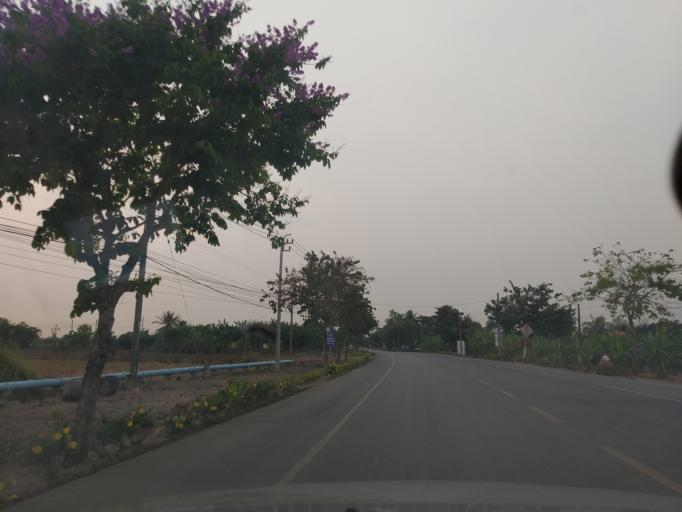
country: TH
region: Bangkok
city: Nong Chok
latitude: 13.8177
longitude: 100.9319
